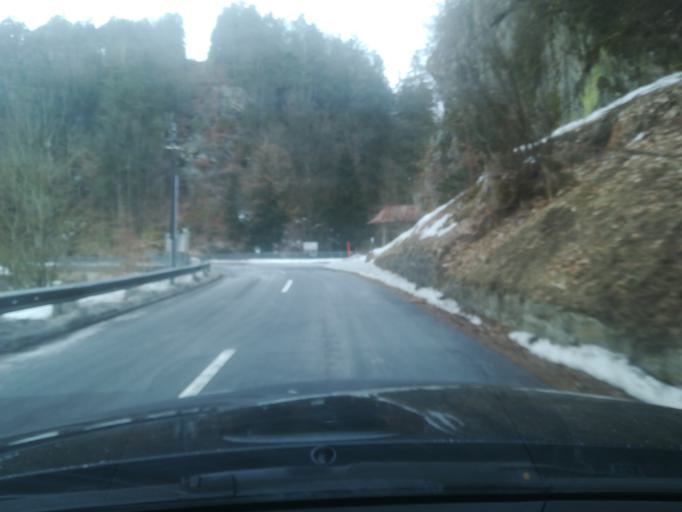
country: AT
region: Upper Austria
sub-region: Politischer Bezirk Perg
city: Perg
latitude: 48.4138
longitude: 14.6406
